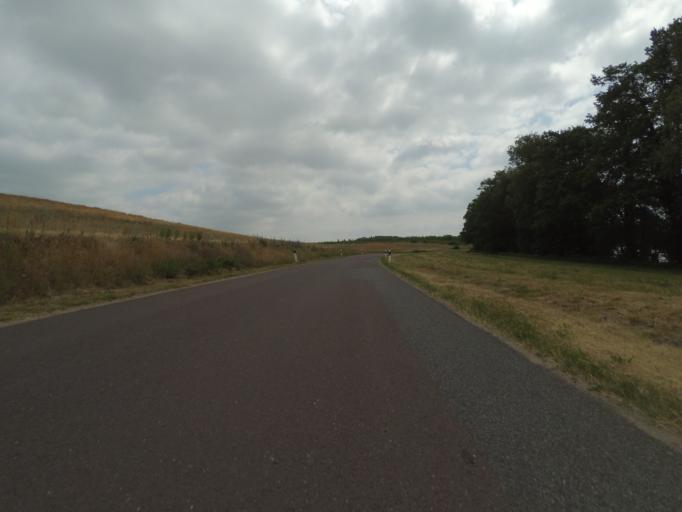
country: DE
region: Mecklenburg-Vorpommern
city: Grabowhofe
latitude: 53.5424
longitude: 12.5568
